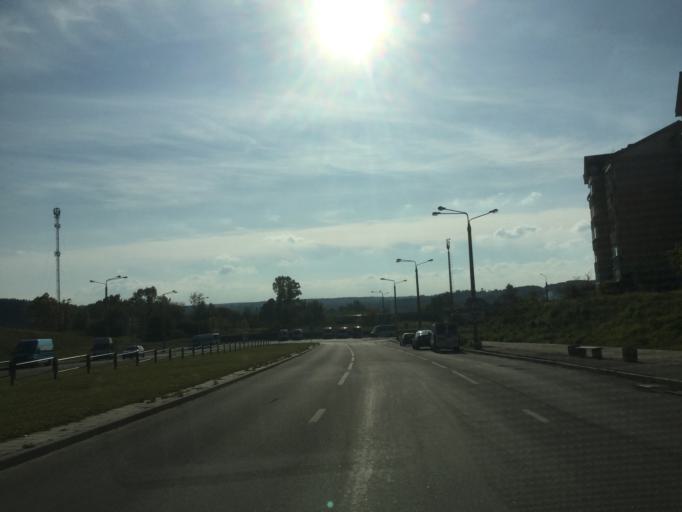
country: BY
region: Vitebsk
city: Vitebsk
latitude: 55.1557
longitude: 30.2111
